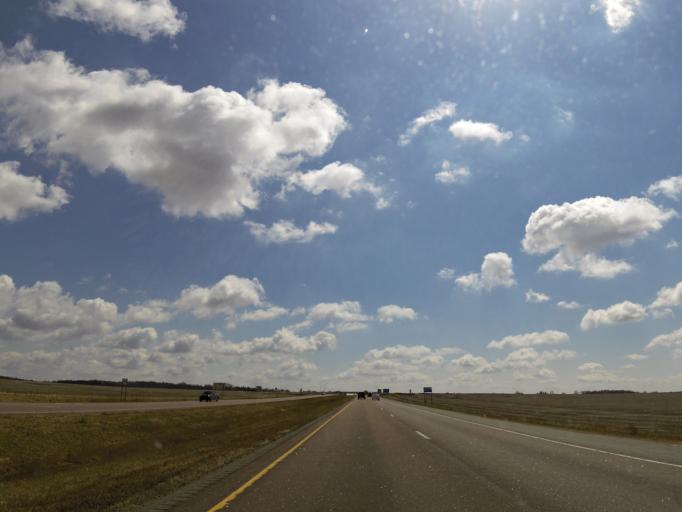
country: US
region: Minnesota
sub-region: Goodhue County
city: Cannon Falls
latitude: 44.6265
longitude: -92.9949
